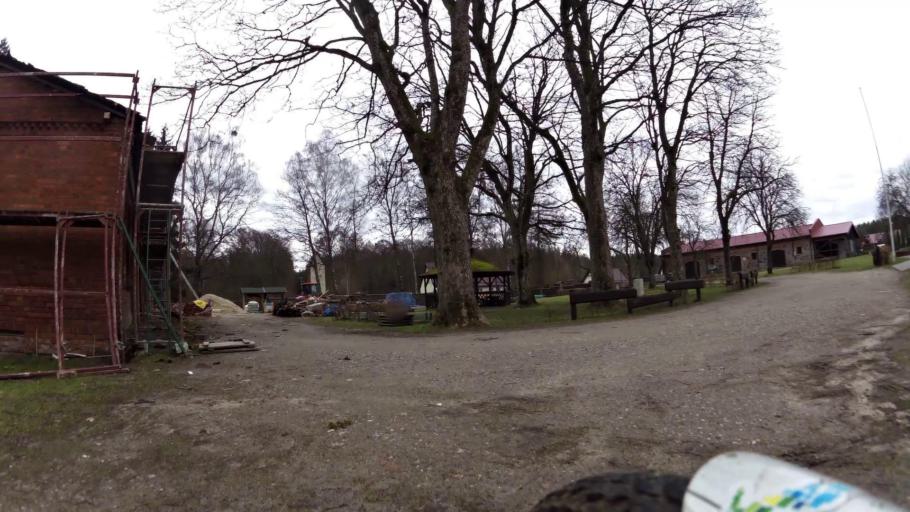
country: PL
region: Pomeranian Voivodeship
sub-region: Powiat bytowski
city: Trzebielino
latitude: 54.1404
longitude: 17.1487
